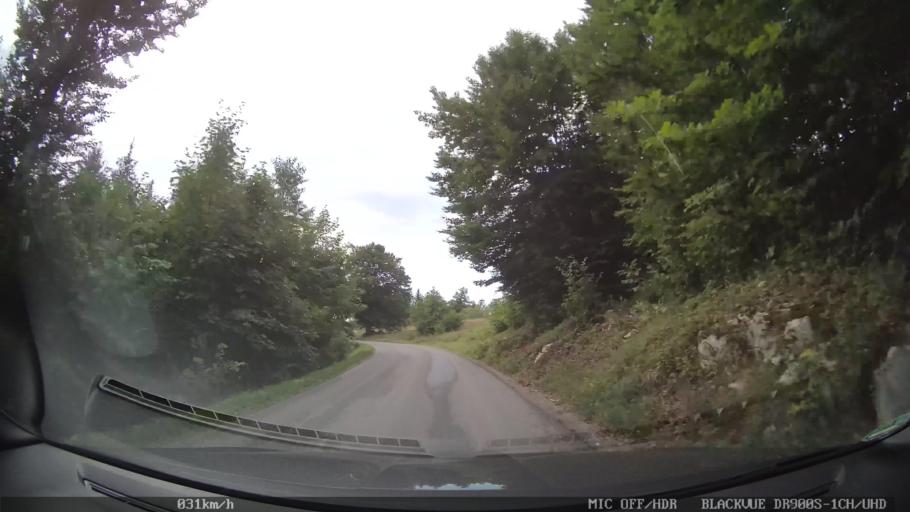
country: HR
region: Licko-Senjska
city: Jezerce
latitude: 44.9423
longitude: 15.5429
